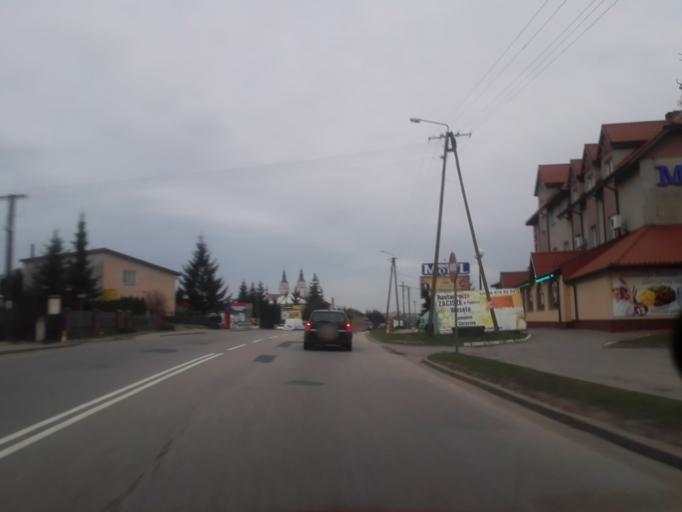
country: PL
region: Podlasie
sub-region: Powiat lomzynski
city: Piatnica
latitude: 53.1991
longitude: 22.0993
